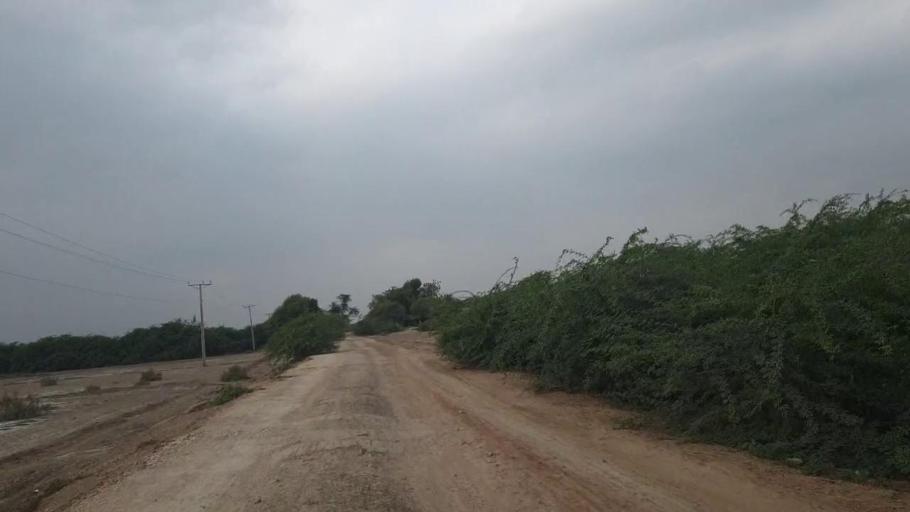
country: PK
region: Sindh
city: Badin
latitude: 24.6158
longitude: 68.6820
